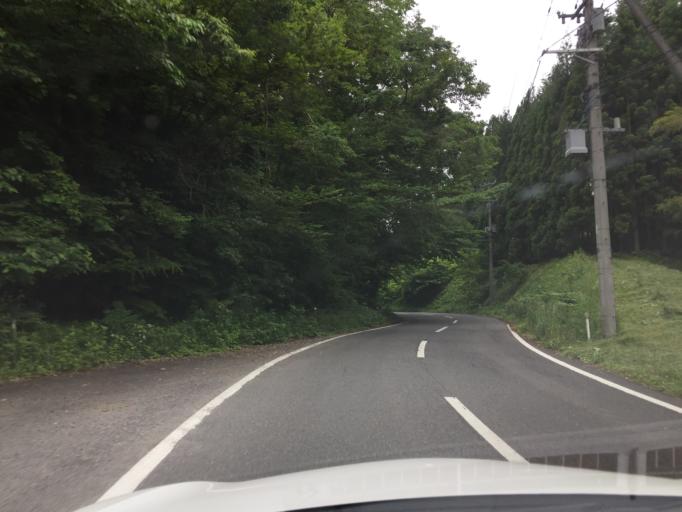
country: JP
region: Fukushima
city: Funehikimachi-funehiki
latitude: 37.2929
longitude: 140.6547
